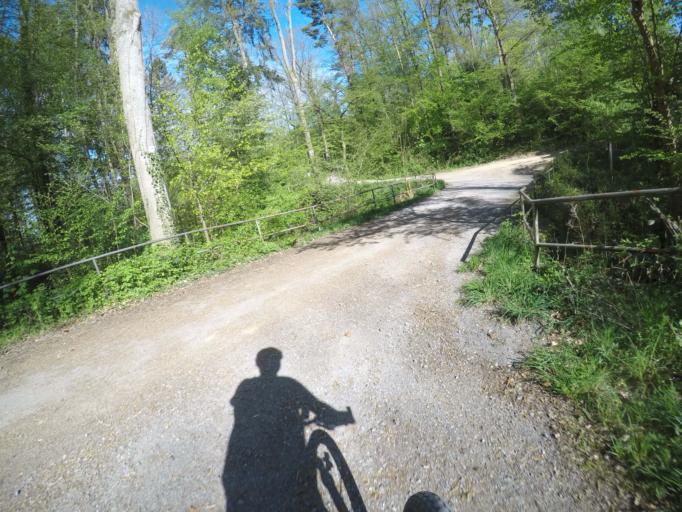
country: DE
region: Baden-Wuerttemberg
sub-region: Regierungsbezirk Stuttgart
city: Stuttgart
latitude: 48.7432
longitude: 9.1454
